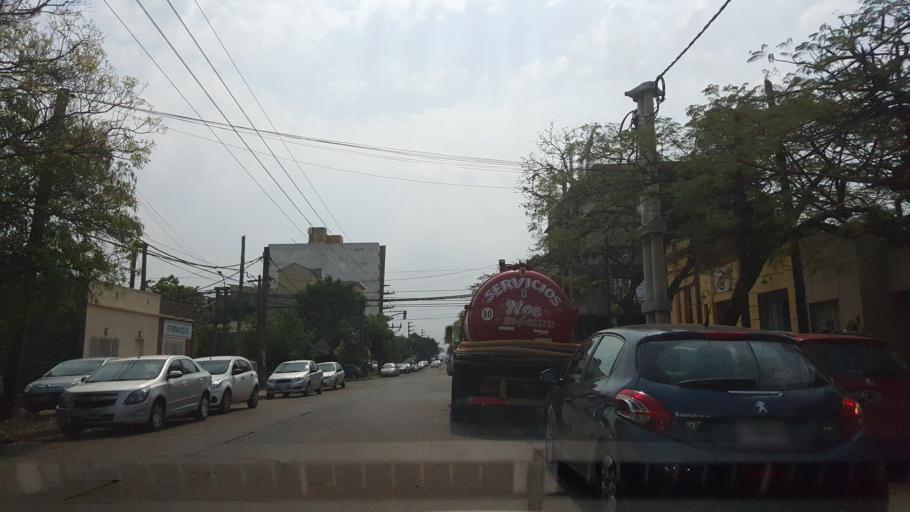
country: AR
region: Misiones
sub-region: Departamento de Capital
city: Posadas
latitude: -27.3669
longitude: -55.9089
